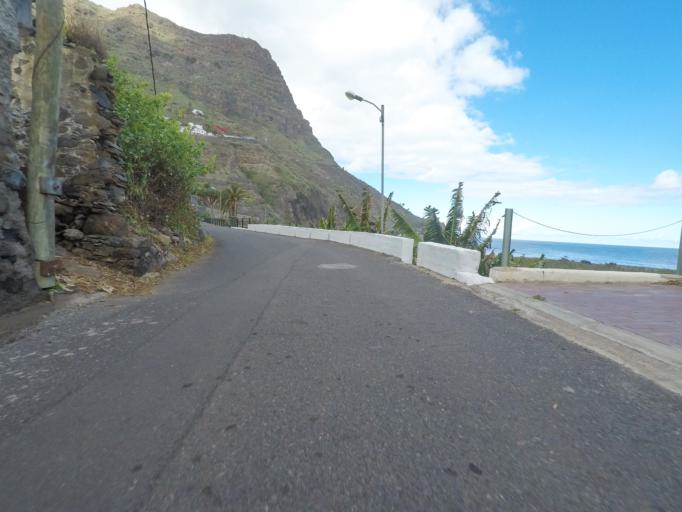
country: ES
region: Canary Islands
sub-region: Provincia de Santa Cruz de Tenerife
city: Hermigua
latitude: 28.1771
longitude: -17.1811
